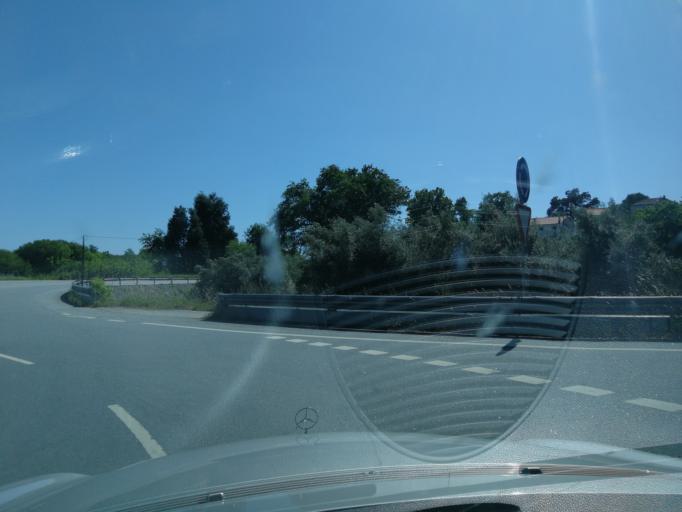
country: PT
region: Viana do Castelo
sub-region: Viana do Castelo
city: Darque
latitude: 41.7170
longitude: -8.7279
